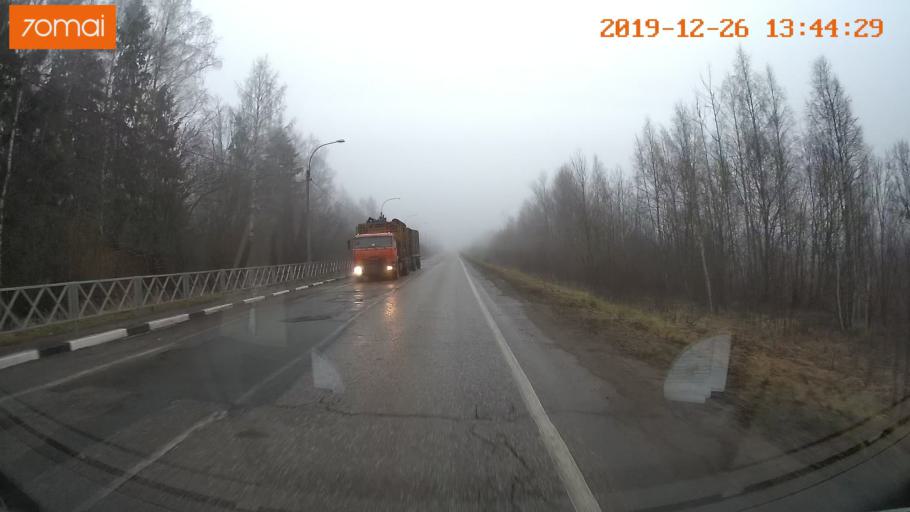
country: RU
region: Vologda
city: Sheksna
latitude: 58.7016
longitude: 38.5070
